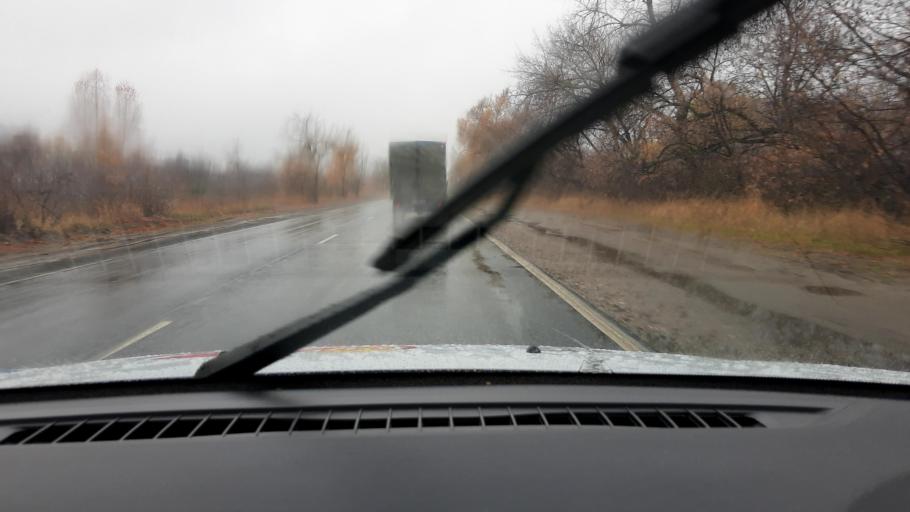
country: RU
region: Nizjnij Novgorod
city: Babino
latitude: 56.2563
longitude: 43.6093
